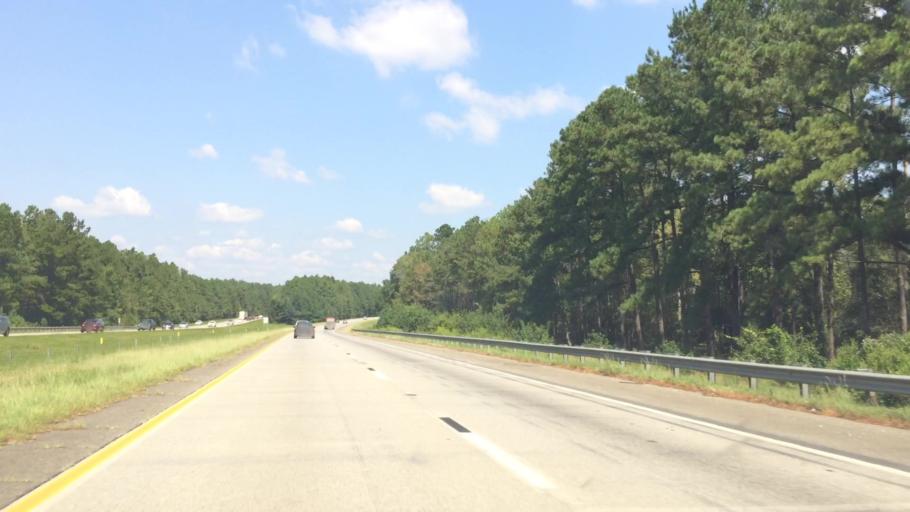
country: US
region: South Carolina
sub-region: Colleton County
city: Walterboro
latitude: 33.0370
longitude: -80.6685
